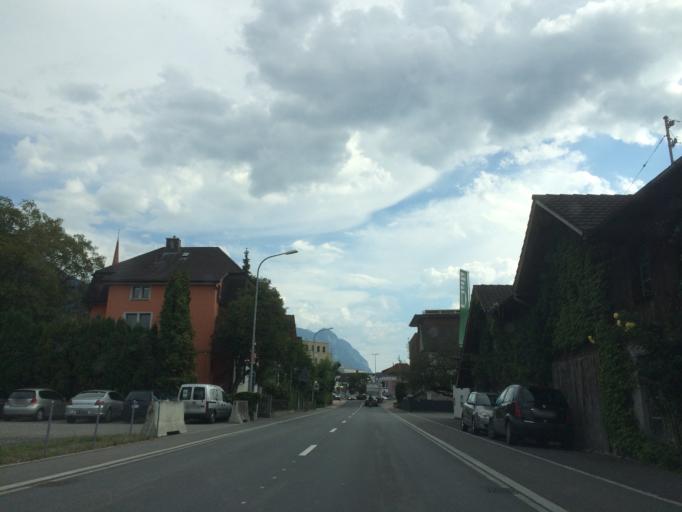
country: LI
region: Schaan
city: Schaan
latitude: 47.1693
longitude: 9.5094
